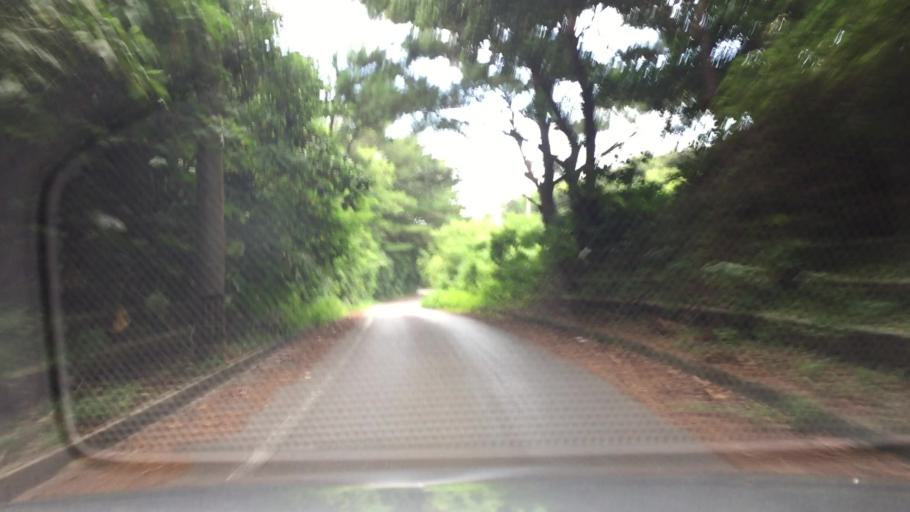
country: JP
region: Okinawa
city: Ishigaki
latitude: 24.4527
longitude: 124.1370
